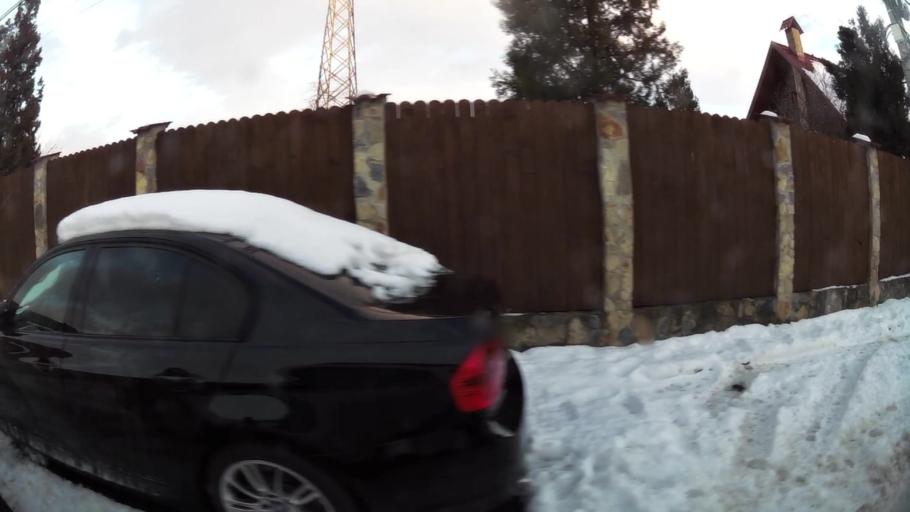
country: RO
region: Ilfov
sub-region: Comuna Popesti-Leordeni
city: Popesti-Leordeni
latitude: 44.3729
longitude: 26.1456
